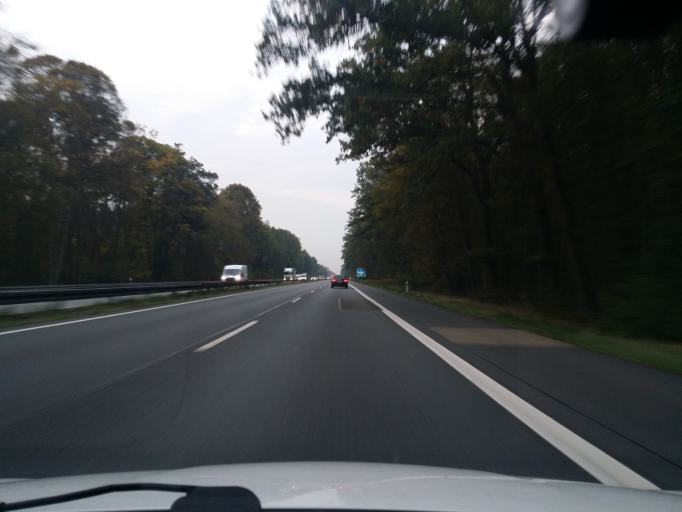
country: DE
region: Hesse
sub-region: Regierungsbezirk Darmstadt
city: Einhausen
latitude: 49.6908
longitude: 8.5514
